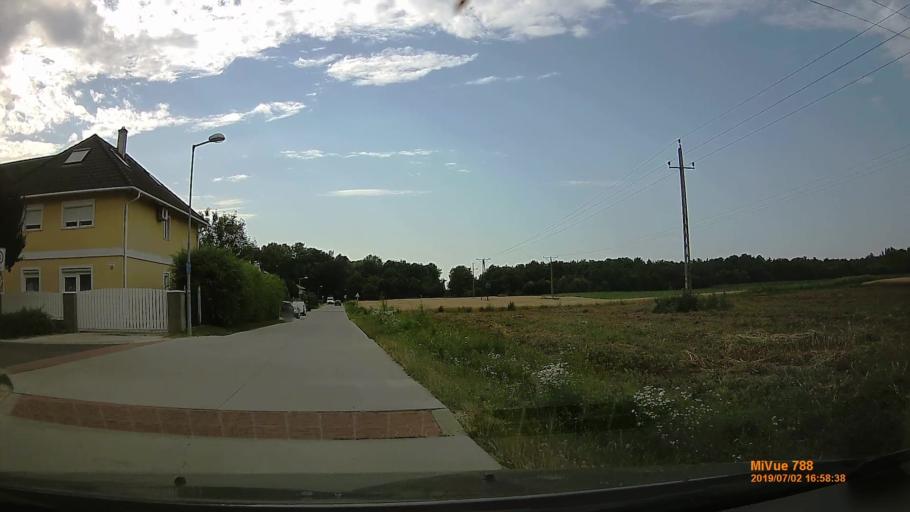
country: HU
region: Gyor-Moson-Sopron
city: Mosonmagyarovar
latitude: 47.8840
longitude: 17.2885
